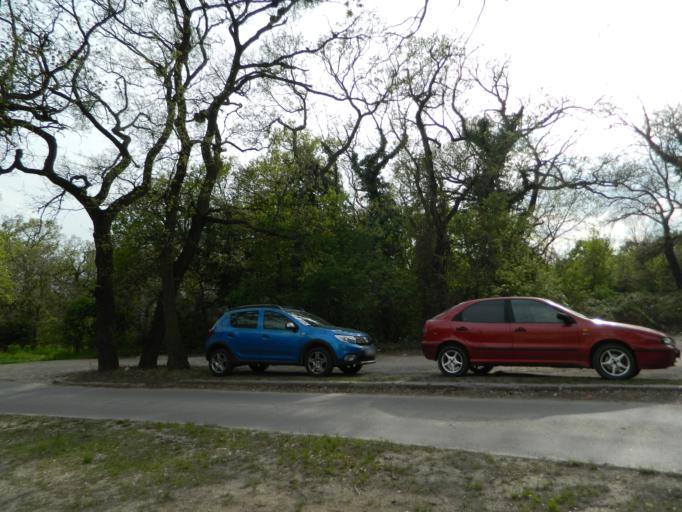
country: HU
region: Veszprem
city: Osi
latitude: 47.2064
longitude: 18.2041
